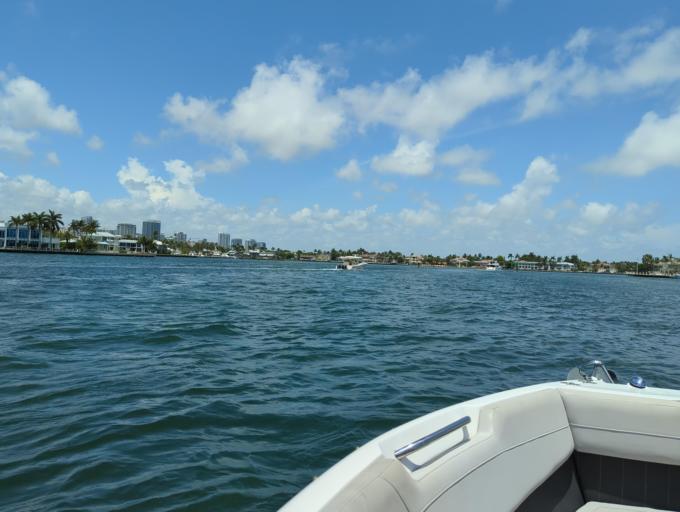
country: US
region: Florida
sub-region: Broward County
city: Fort Lauderdale
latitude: 26.1044
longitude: -80.1195
